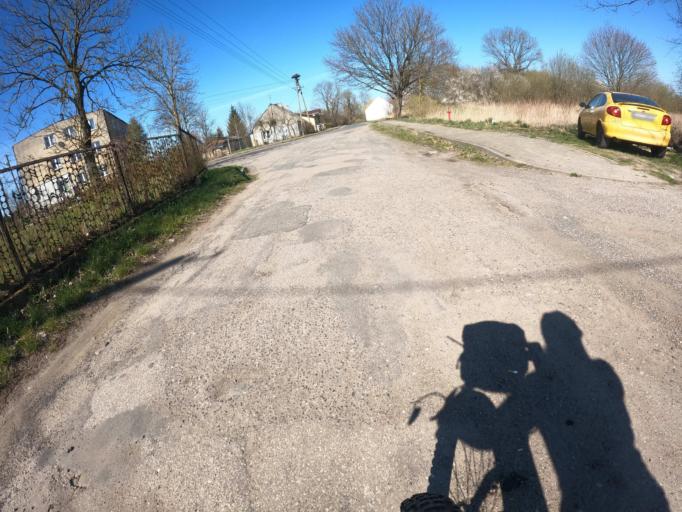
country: PL
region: West Pomeranian Voivodeship
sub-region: Powiat gryficki
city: Brojce
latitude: 54.0007
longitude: 15.3877
